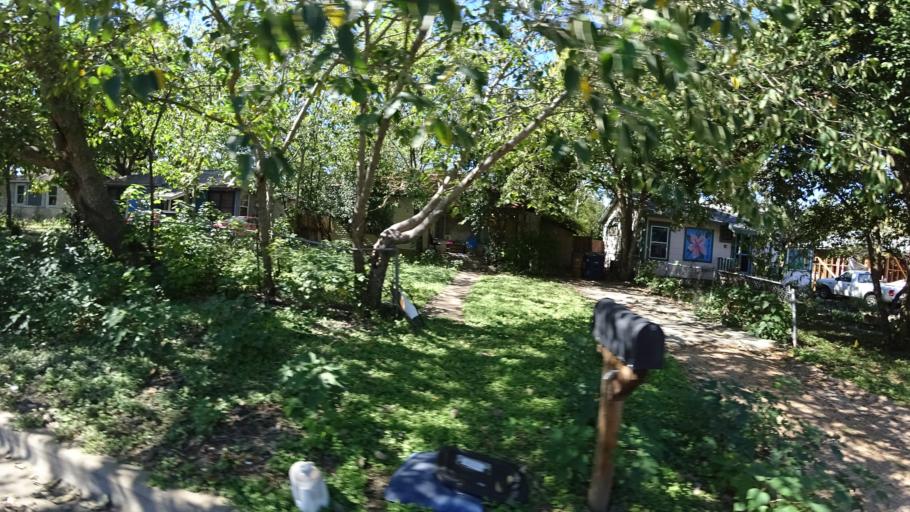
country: US
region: Texas
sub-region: Travis County
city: Rollingwood
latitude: 30.2231
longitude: -97.7794
